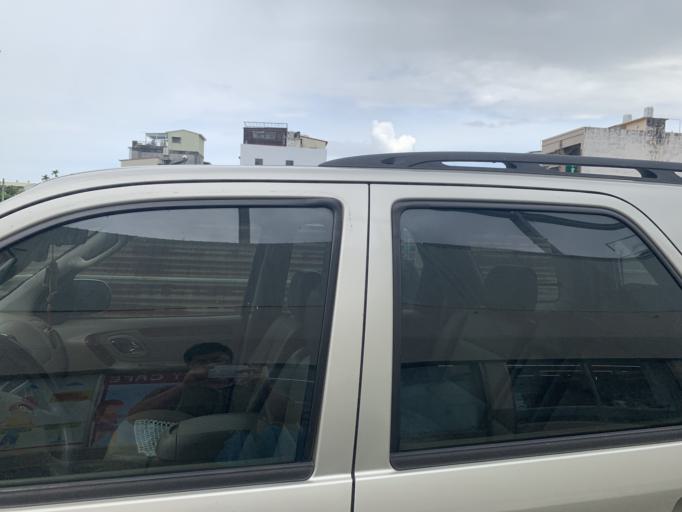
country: TW
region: Taiwan
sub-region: Chiayi
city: Jiayi Shi
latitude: 23.4921
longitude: 120.4770
